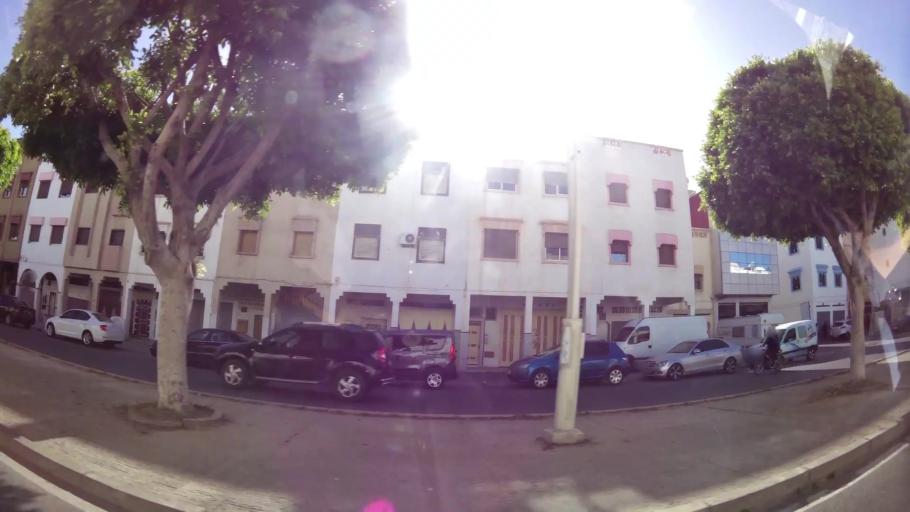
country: MA
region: Oued ed Dahab-Lagouira
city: Dakhla
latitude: 30.4097
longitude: -9.5674
